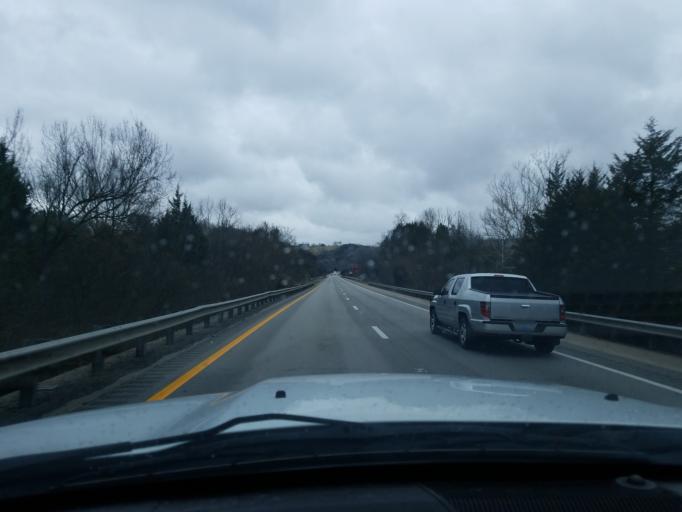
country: US
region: Kentucky
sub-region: Franklin County
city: Frankfort
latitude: 38.1637
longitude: -84.8478
